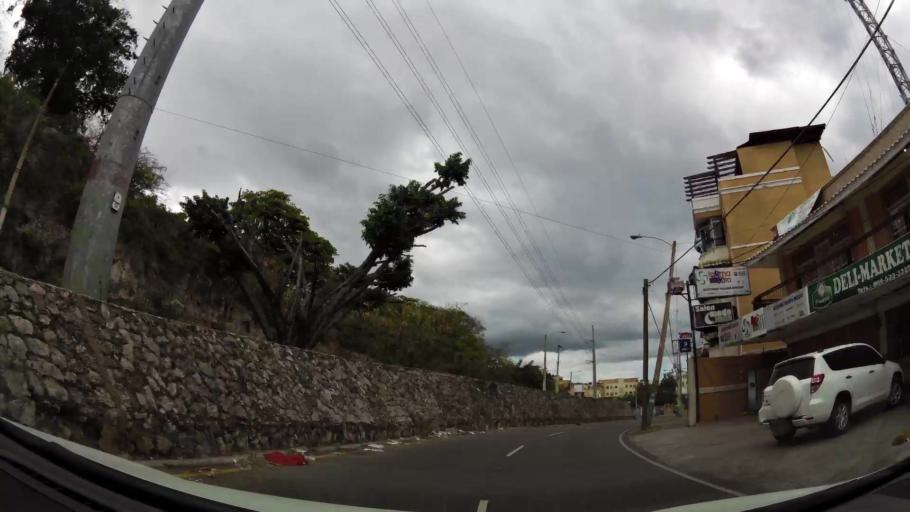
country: DO
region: Nacional
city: Bella Vista
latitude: 18.4411
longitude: -69.9574
